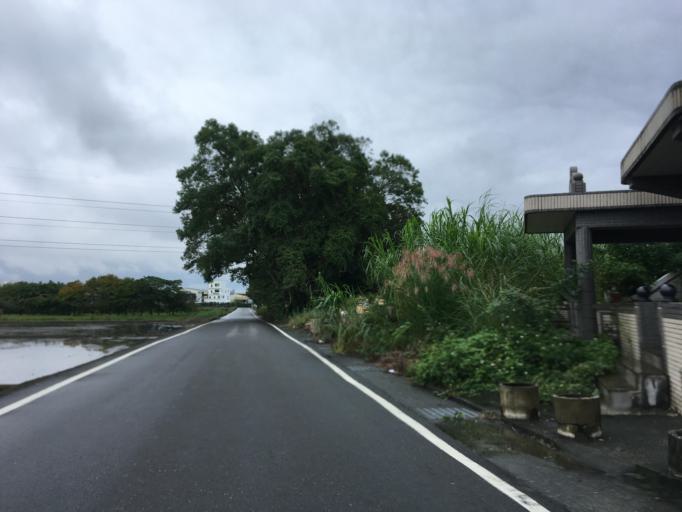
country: TW
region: Taiwan
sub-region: Yilan
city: Yilan
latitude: 24.6637
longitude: 121.7469
